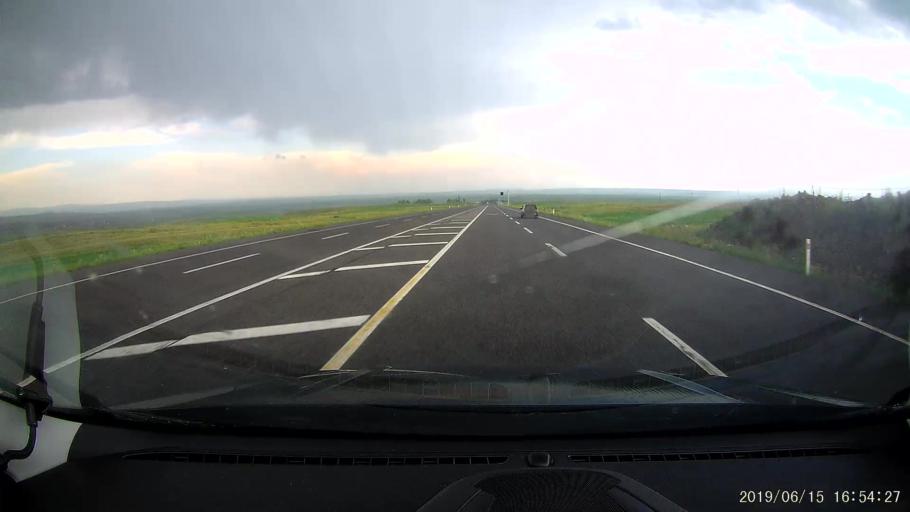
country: TR
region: Kars
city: Susuz
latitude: 40.7903
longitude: 43.1244
